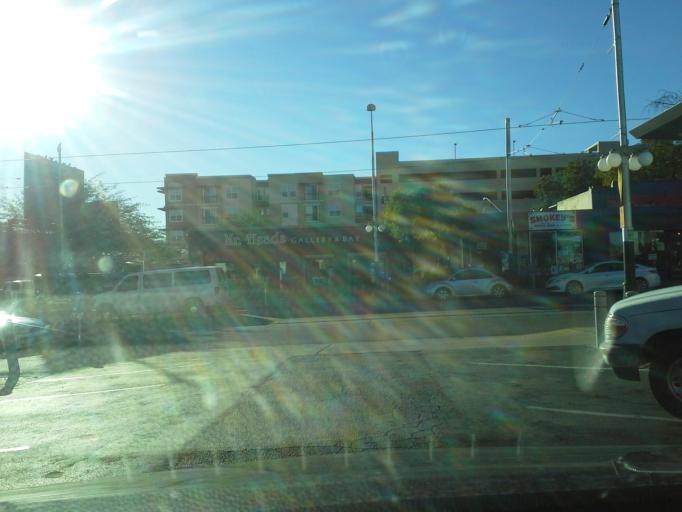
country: US
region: Arizona
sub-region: Pima County
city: South Tucson
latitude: 32.2282
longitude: -110.9654
